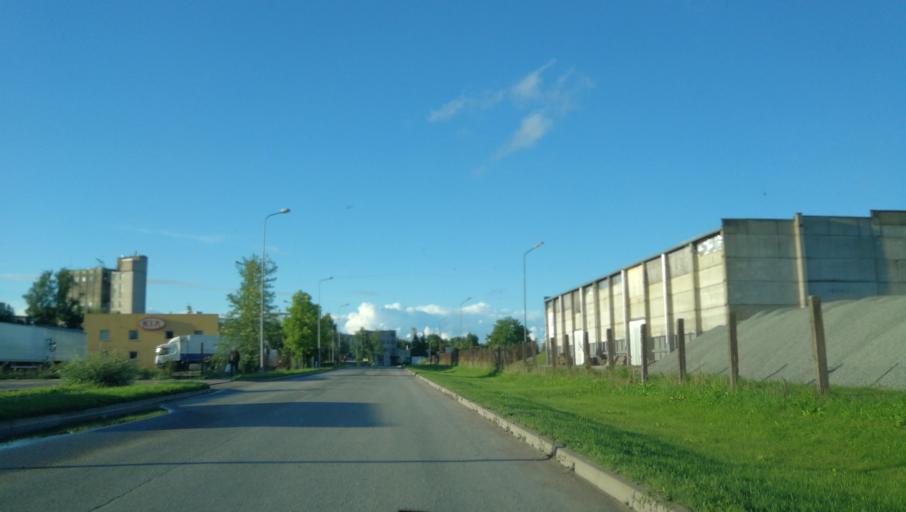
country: LV
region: Valmieras Rajons
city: Valmiera
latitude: 57.5155
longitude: 25.4402
